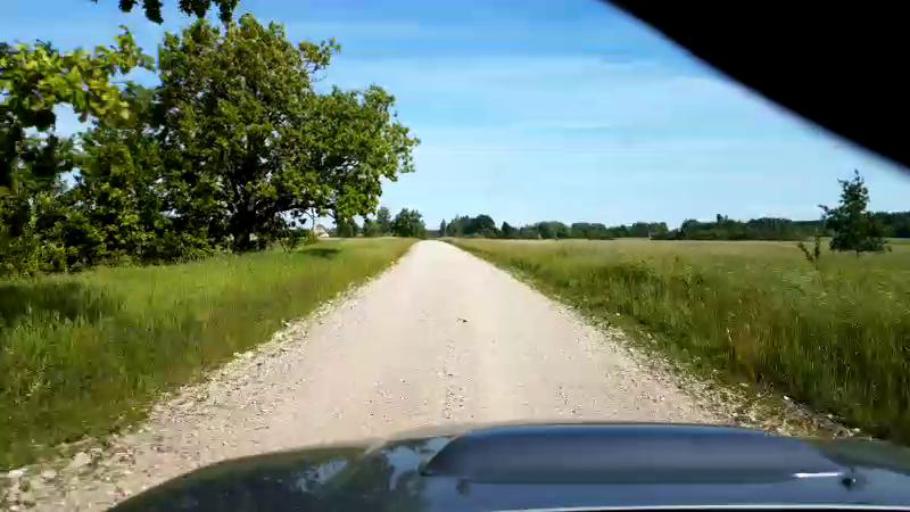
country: EE
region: Paernumaa
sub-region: Sauga vald
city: Sauga
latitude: 58.4793
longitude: 24.5312
